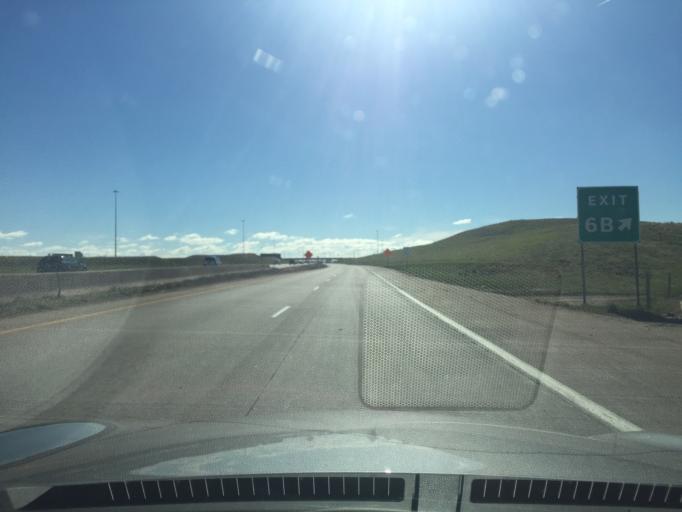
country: US
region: Colorado
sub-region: Adams County
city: Aurora
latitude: 39.8337
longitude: -104.7451
